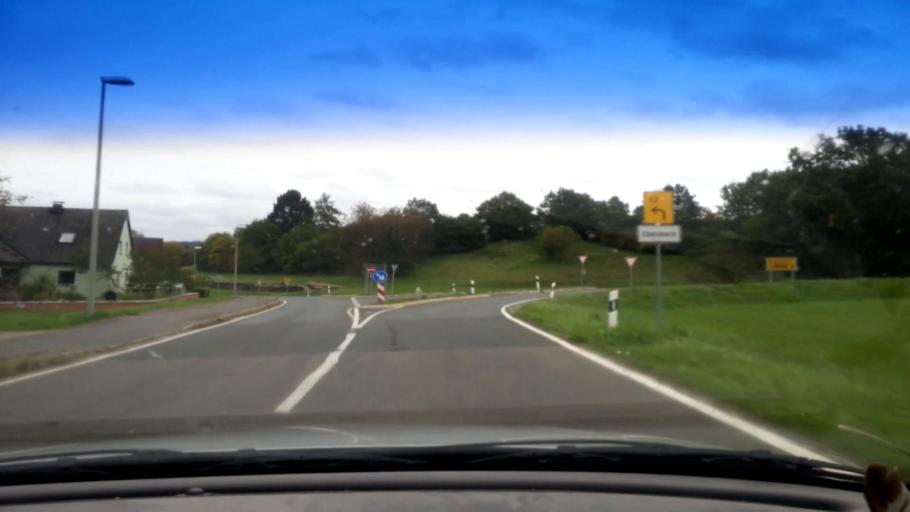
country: DE
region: Bavaria
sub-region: Upper Franconia
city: Lauter
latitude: 49.9683
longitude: 10.7951
